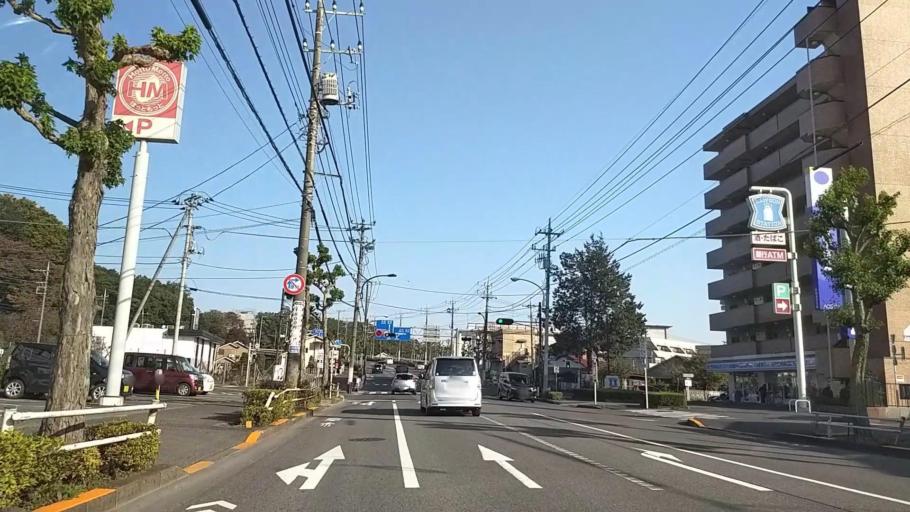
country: JP
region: Tokyo
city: Ome
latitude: 35.7864
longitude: 139.2724
